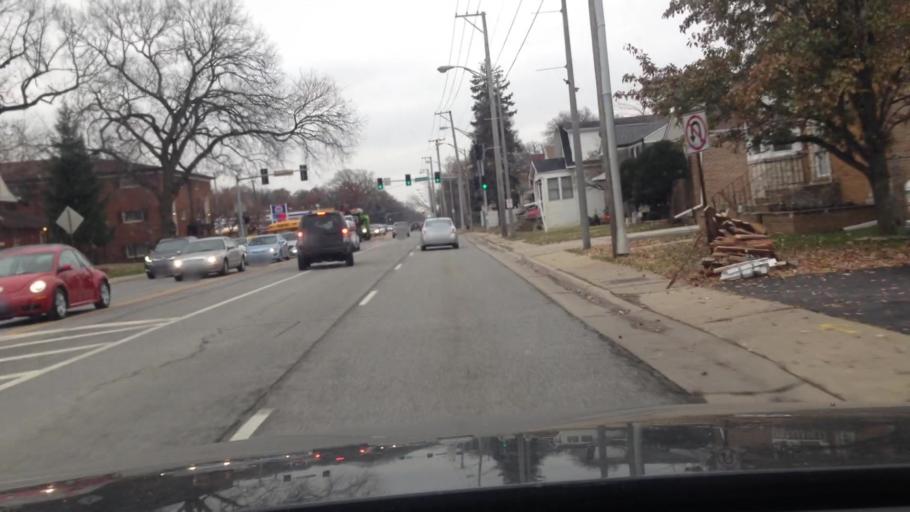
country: US
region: Illinois
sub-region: Cook County
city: River Grove
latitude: 41.9266
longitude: -87.8358
